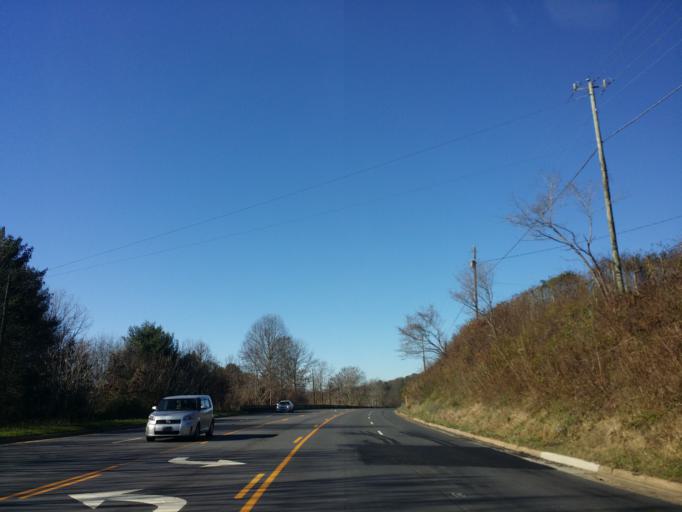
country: US
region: North Carolina
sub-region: Buncombe County
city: Swannanoa
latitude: 35.5914
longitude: -82.4423
